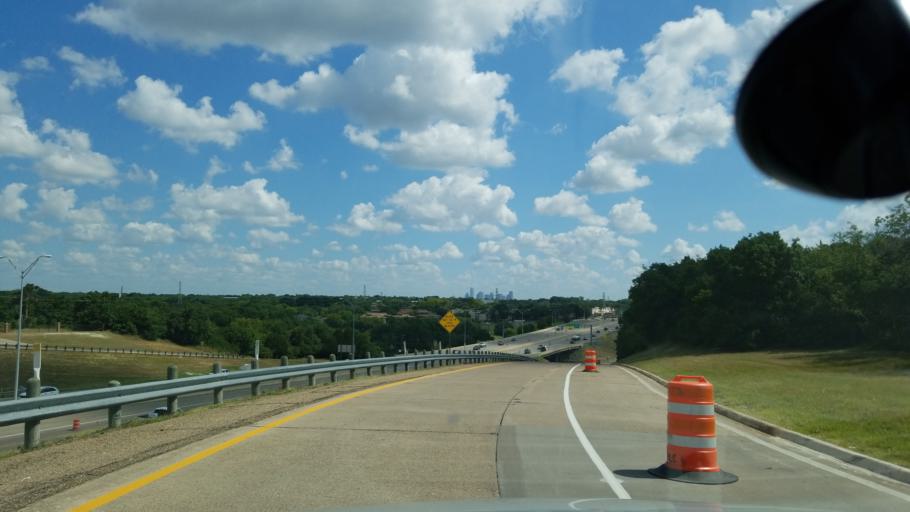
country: US
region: Texas
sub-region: Dallas County
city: Cockrell Hill
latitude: 32.6934
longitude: -96.8443
